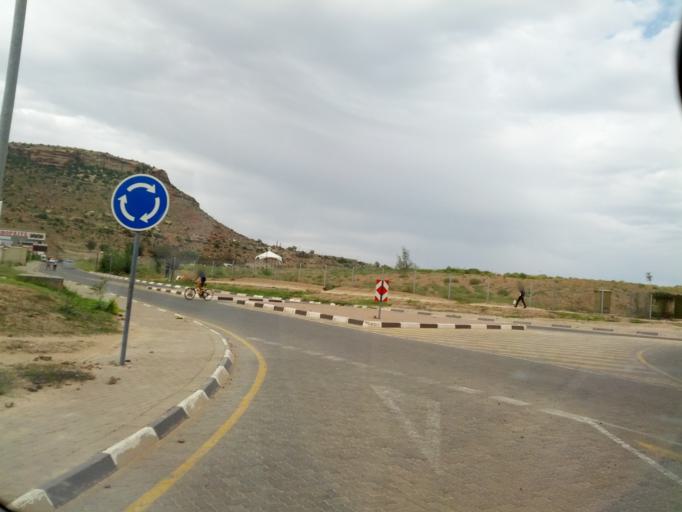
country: LS
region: Maseru
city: Maseru
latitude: -29.3326
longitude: 27.4826
